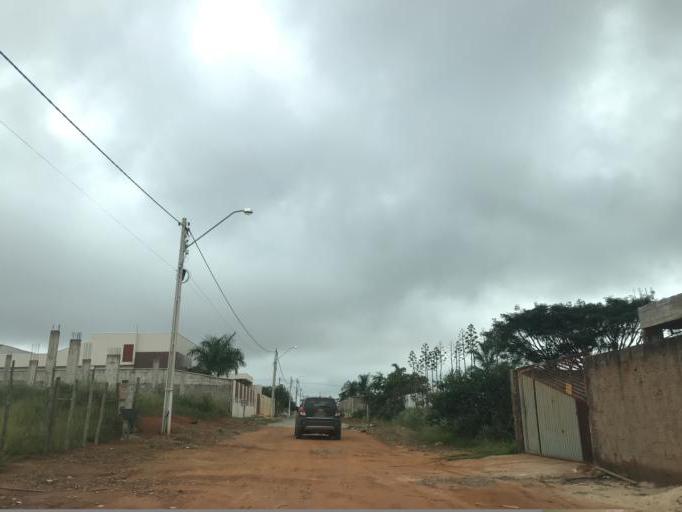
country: BR
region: Federal District
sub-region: Brasilia
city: Brasilia
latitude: -15.8299
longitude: -47.7920
